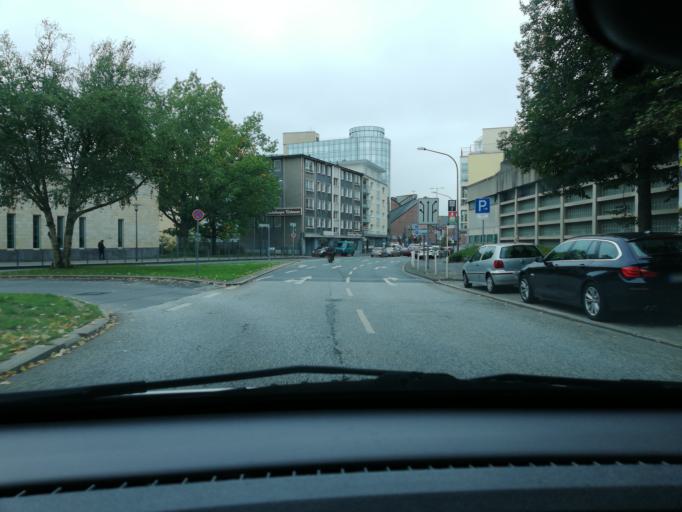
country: DE
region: North Rhine-Westphalia
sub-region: Regierungsbezirk Dusseldorf
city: Wuppertal
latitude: 51.2722
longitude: 7.1974
